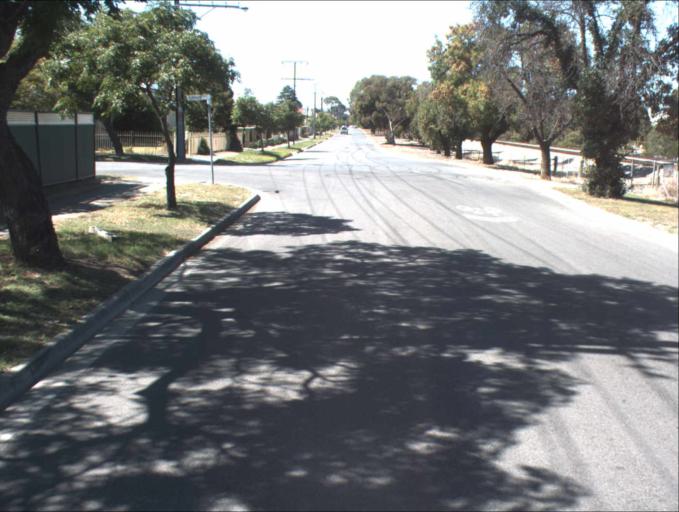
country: AU
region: South Australia
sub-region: Port Adelaide Enfield
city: Alberton
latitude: -34.8615
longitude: 138.5213
